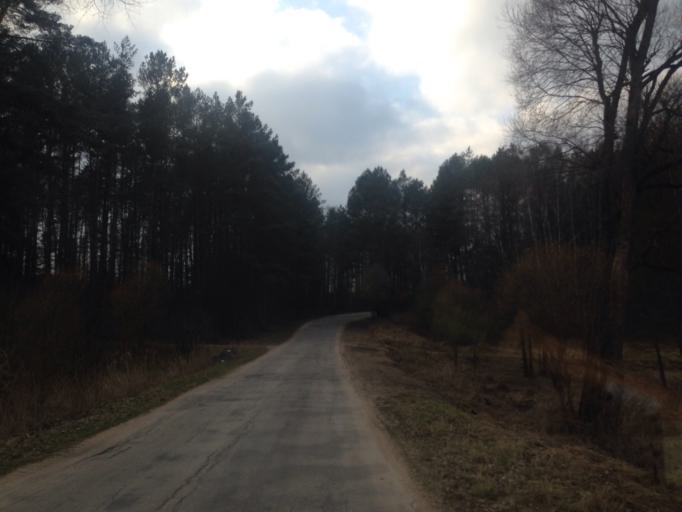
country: PL
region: Warmian-Masurian Voivodeship
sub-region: Powiat dzialdowski
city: Lidzbark
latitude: 53.3469
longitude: 19.7375
